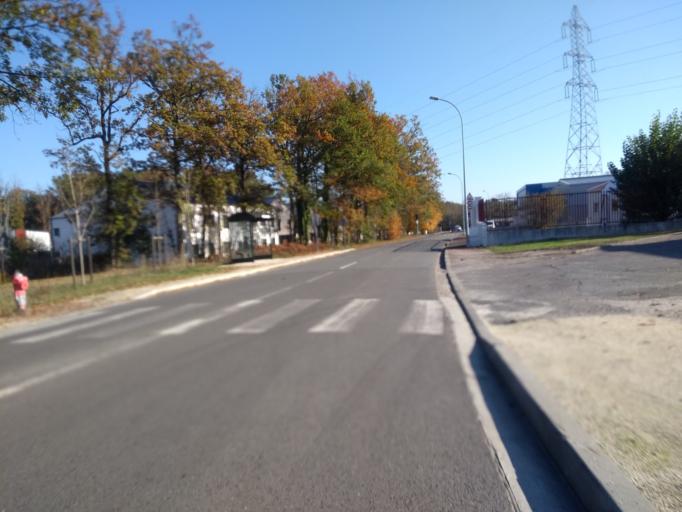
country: FR
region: Aquitaine
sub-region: Departement de la Gironde
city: Leognan
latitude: 44.7420
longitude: -0.6125
